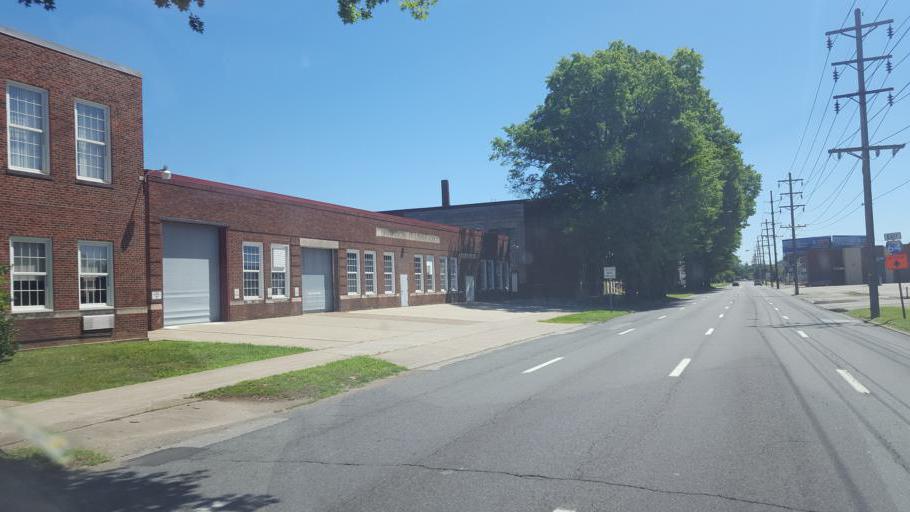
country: US
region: West Virginia
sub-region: Cabell County
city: Huntington
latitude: 38.4268
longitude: -82.4010
